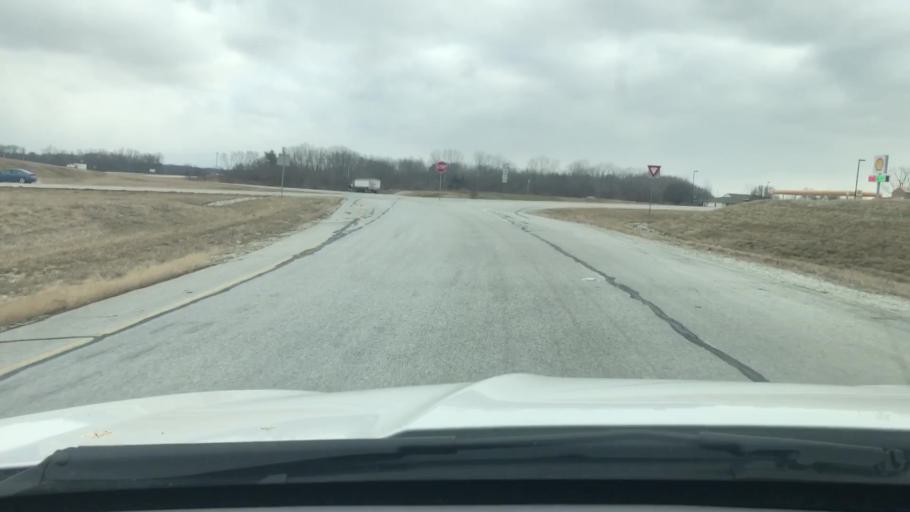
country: US
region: Indiana
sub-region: Carroll County
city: Delphi
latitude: 40.5662
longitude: -86.6587
